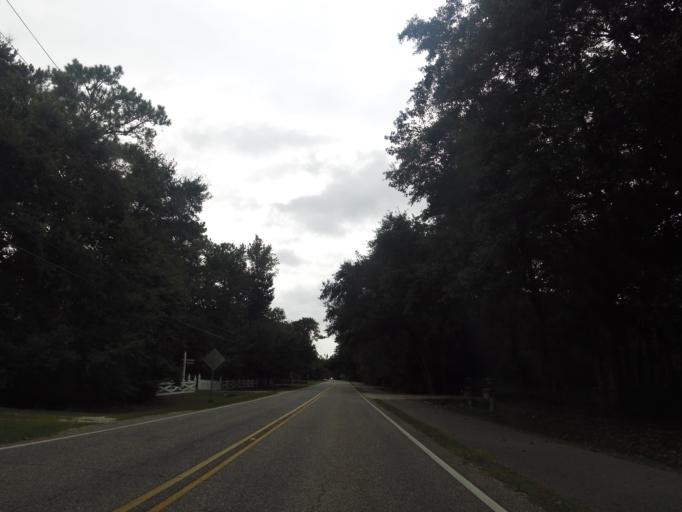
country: US
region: Alabama
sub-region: Baldwin County
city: Point Clear
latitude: 30.4787
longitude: -87.9234
